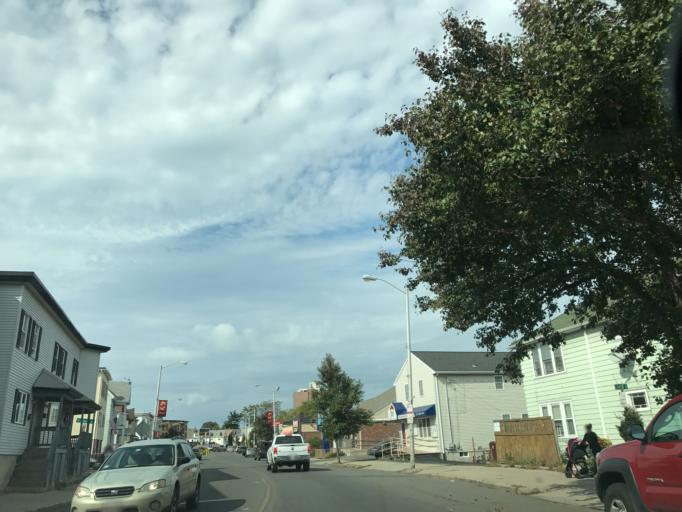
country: US
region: Massachusetts
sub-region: Middlesex County
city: Everett
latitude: 42.4135
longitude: -71.0463
